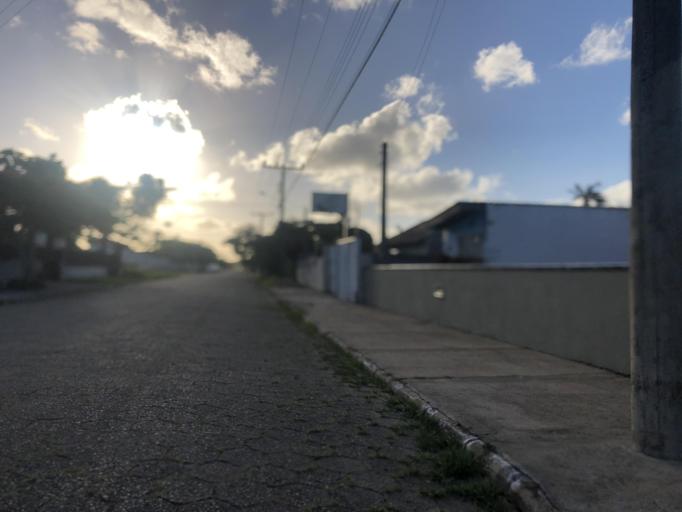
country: BR
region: Santa Catarina
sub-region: Sao Francisco Do Sul
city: Sao Francisco do Sul
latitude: -26.2173
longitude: -48.5269
